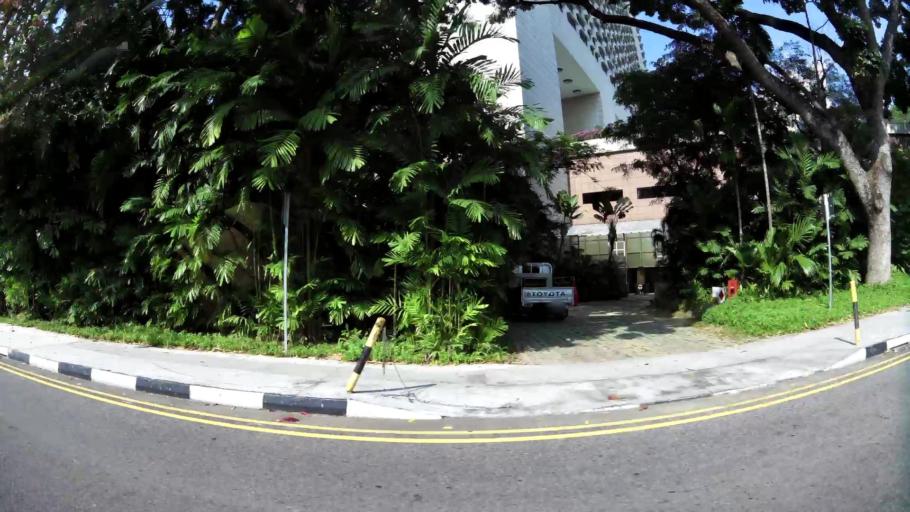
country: SG
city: Singapore
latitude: 1.2904
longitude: 103.8608
